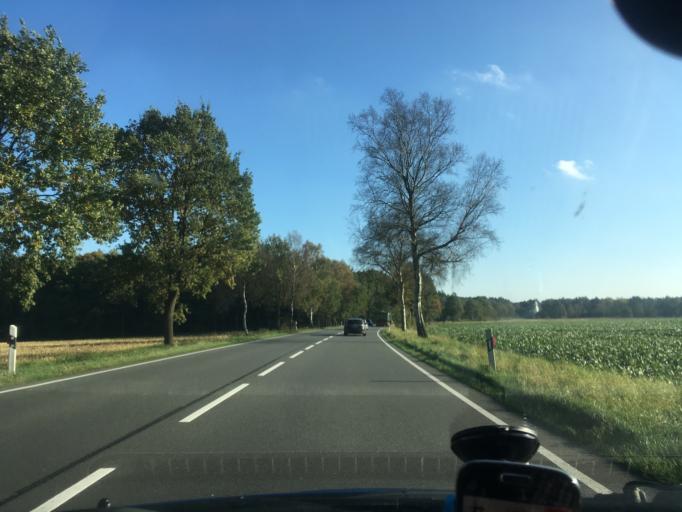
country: DE
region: Lower Saxony
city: Wietzendorf
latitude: 52.9285
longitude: 9.9052
